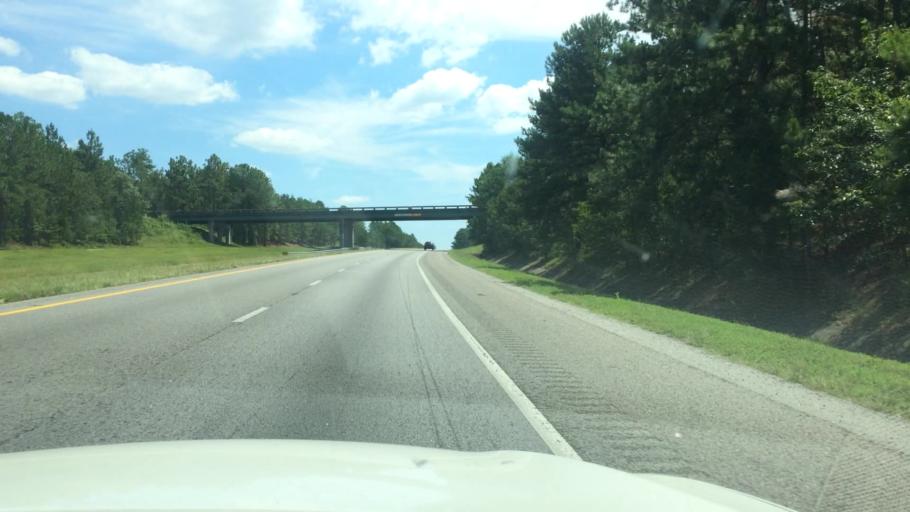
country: US
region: South Carolina
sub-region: Aiken County
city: Aiken
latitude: 33.7027
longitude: -81.6012
